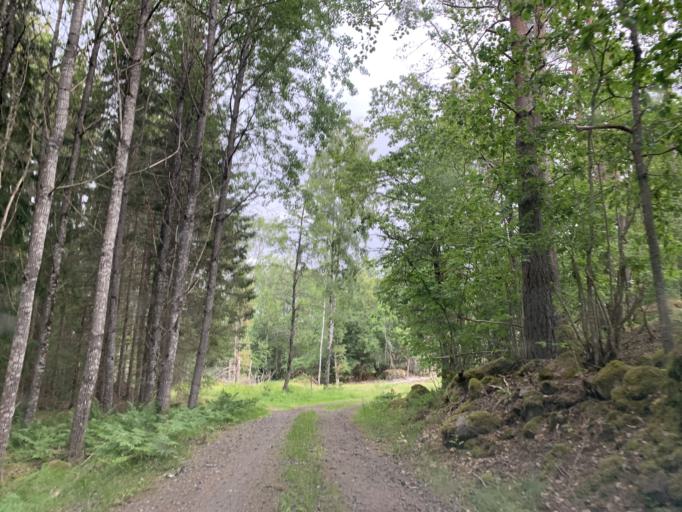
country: SE
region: Kalmar
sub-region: Vasterviks Kommun
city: Overum
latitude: 58.0269
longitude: 16.1174
